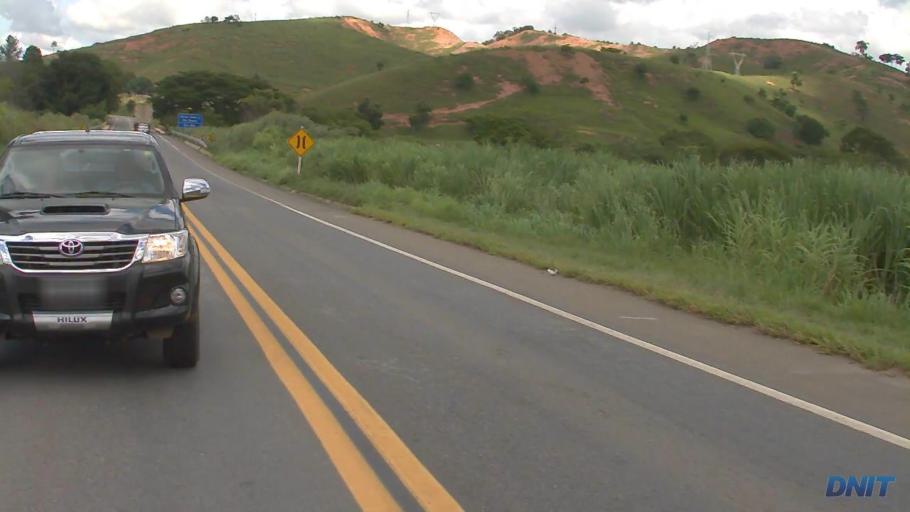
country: BR
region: Minas Gerais
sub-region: Governador Valadares
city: Governador Valadares
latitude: -18.9600
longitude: -42.0758
